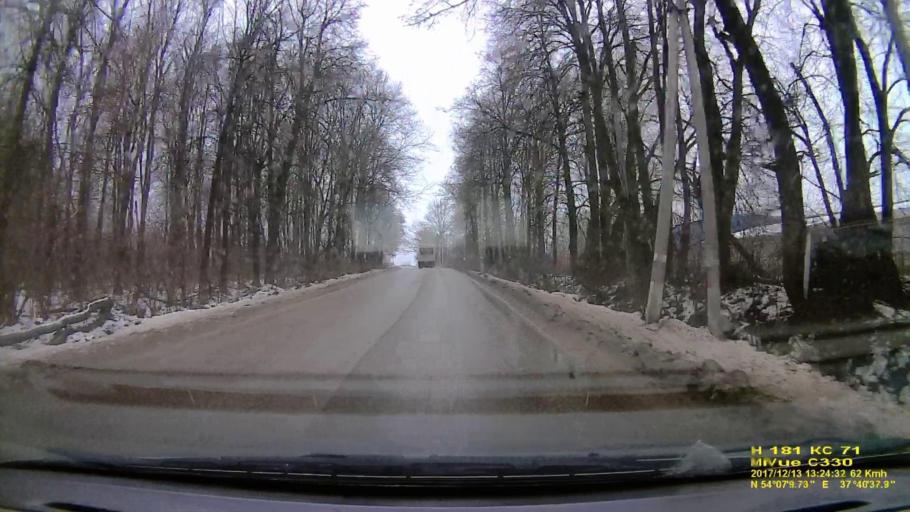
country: RU
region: Tula
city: Skuratovskiy
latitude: 54.1193
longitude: 37.6770
